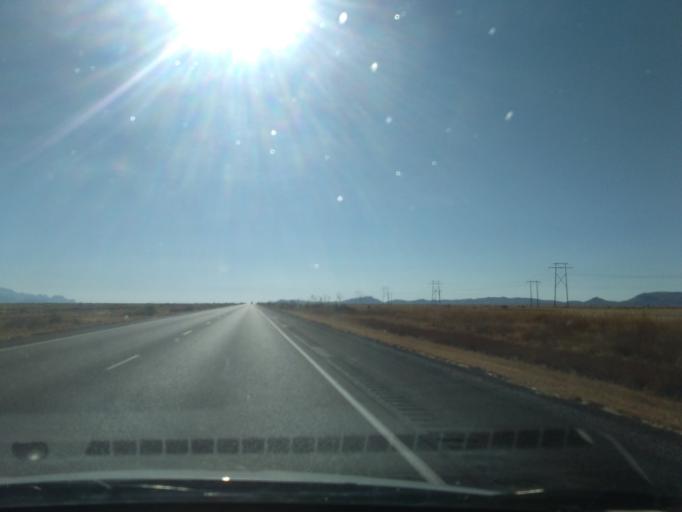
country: US
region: New Mexico
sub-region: Luna County
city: Deming
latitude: 32.4733
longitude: -107.5337
